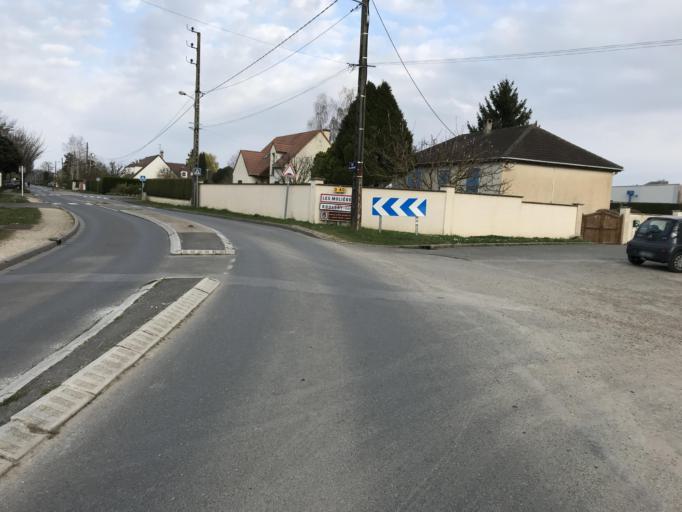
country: FR
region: Ile-de-France
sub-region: Departement de l'Essonne
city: Les Molieres
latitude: 48.6686
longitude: 2.0524
